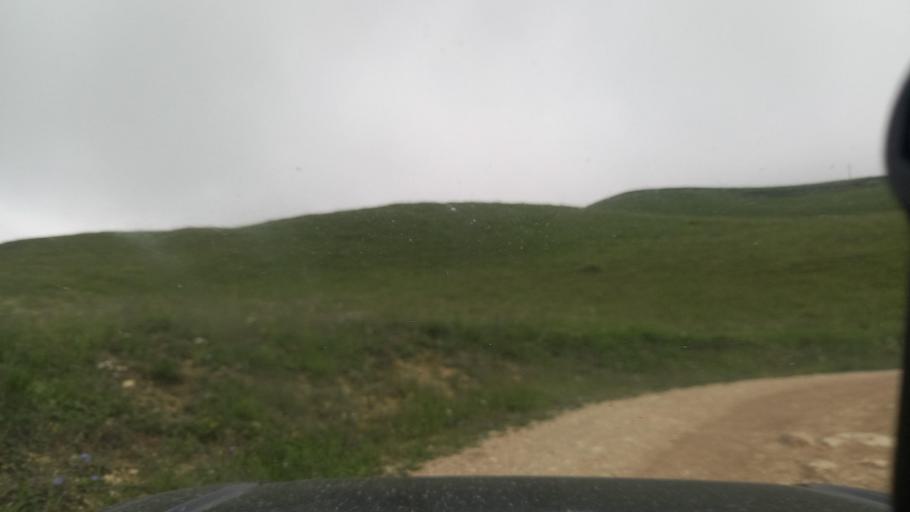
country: RU
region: Karachayevo-Cherkesiya
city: Pregradnaya
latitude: 44.0091
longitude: 41.1671
